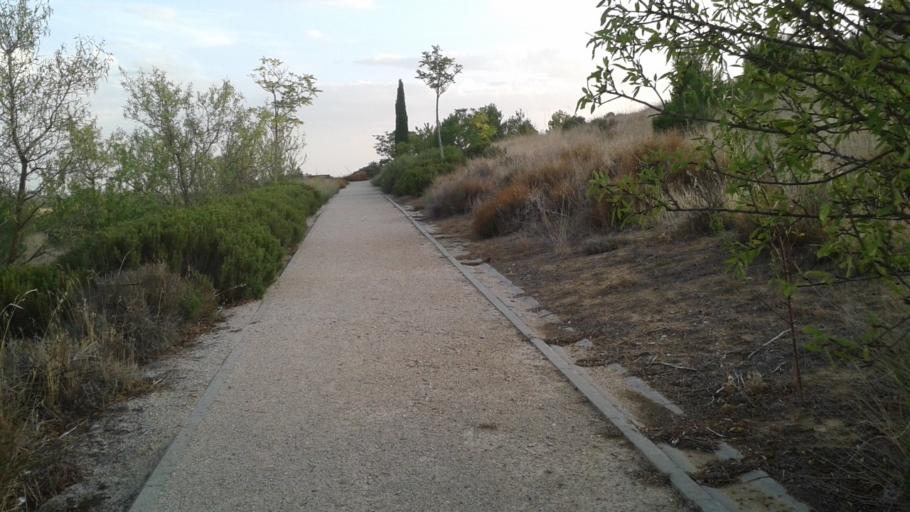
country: ES
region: Castille and Leon
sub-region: Provincia de Valladolid
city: Arroyo
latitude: 41.6158
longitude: -4.7864
